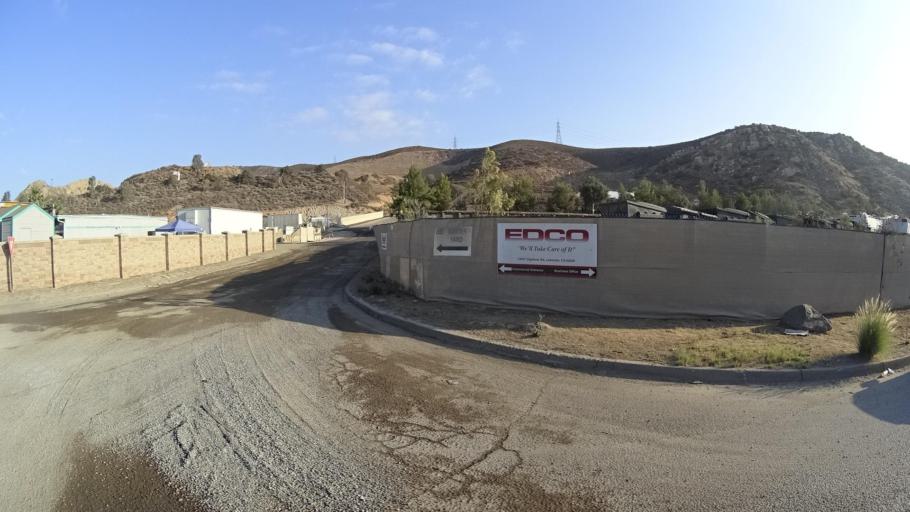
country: US
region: California
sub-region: San Diego County
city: Eucalyptus Hills
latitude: 32.9052
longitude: -116.9388
